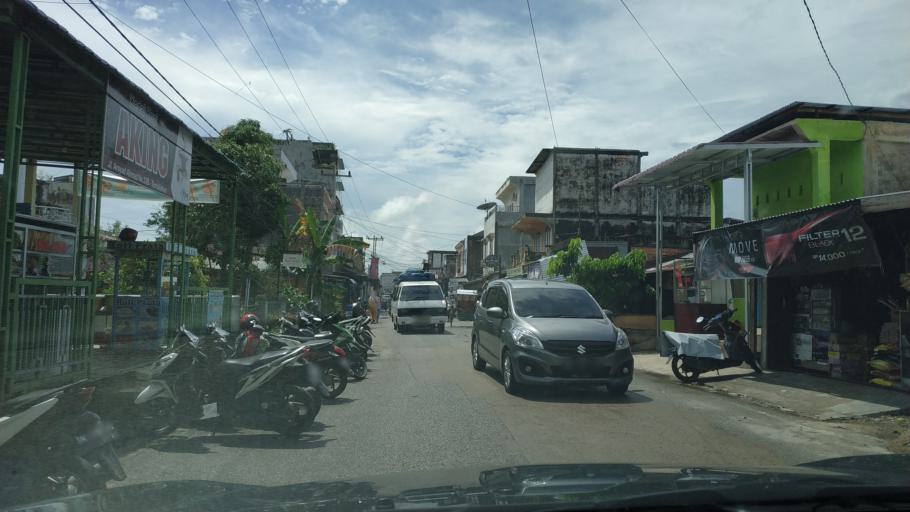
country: ID
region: Riau
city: Tembilahan
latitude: -0.3221
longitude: 103.1541
